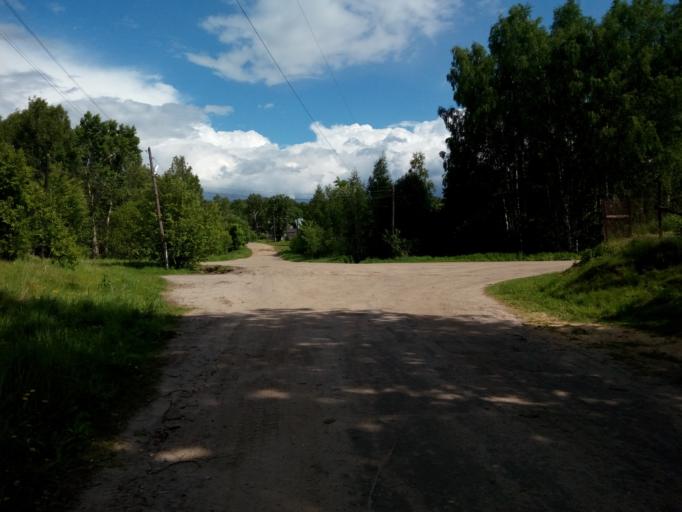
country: RU
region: Nizjnij Novgorod
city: Voskresenskoye
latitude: 56.7805
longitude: 45.5259
